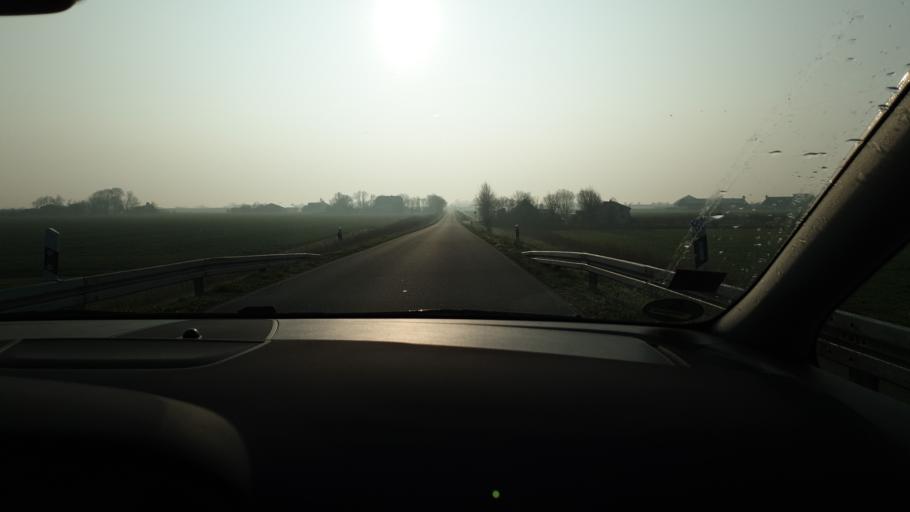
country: DE
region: Schleswig-Holstein
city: Elisabeth-Sophien-Koog
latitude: 54.4989
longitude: 8.8962
